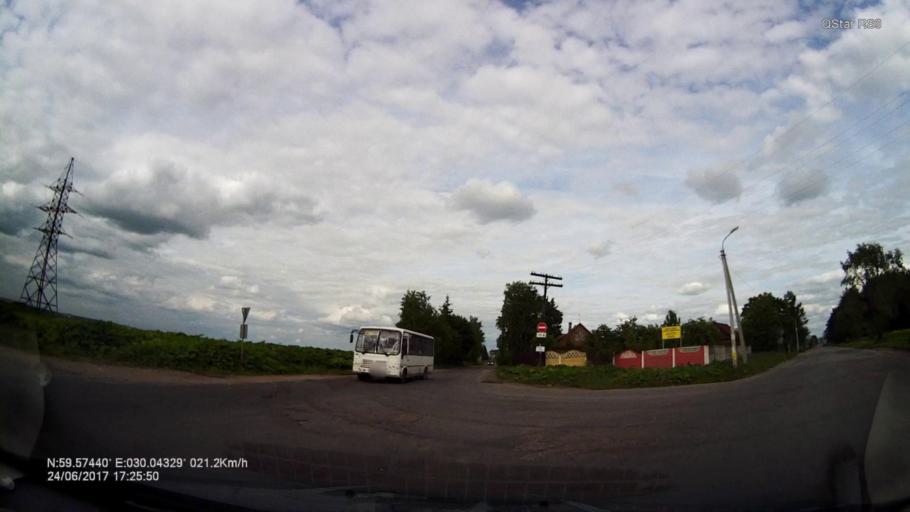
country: RU
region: Leningrad
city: Mariyenburg
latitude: 59.5744
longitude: 30.0435
